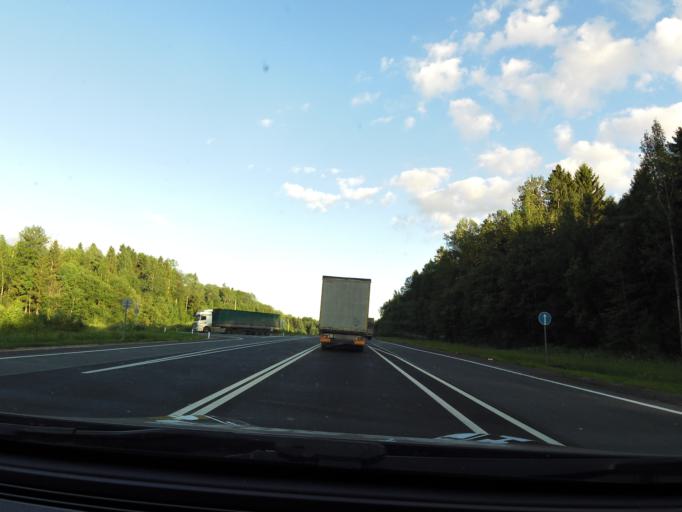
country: RU
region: Vologda
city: Gryazovets
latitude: 58.9773
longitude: 40.1481
